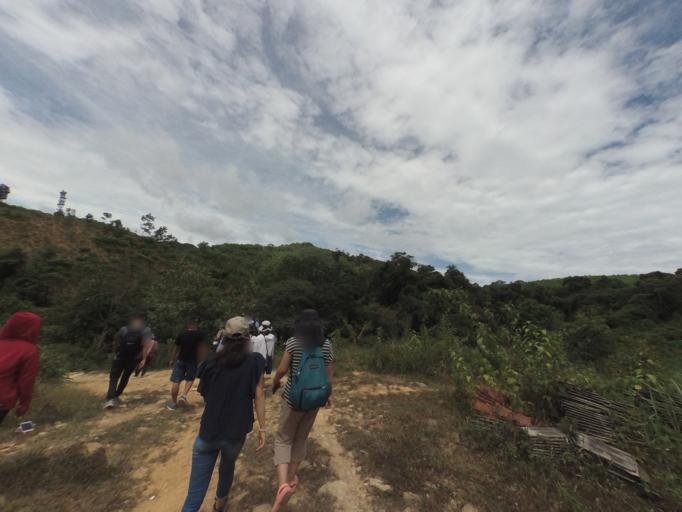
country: VN
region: Thua Thien-Hue
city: A Luoi
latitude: 16.3061
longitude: 107.2138
